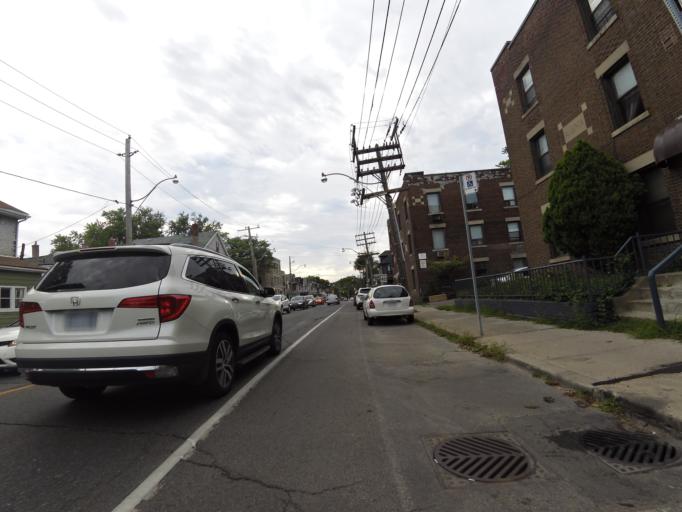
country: CA
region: Ontario
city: Toronto
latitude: 43.6667
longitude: -79.3322
